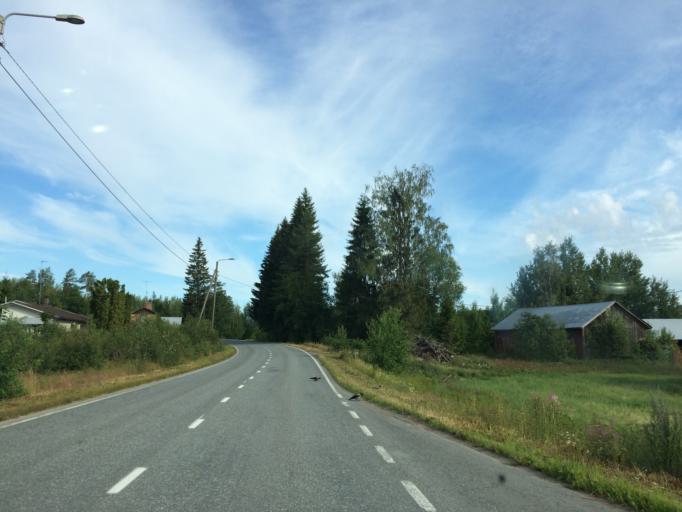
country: FI
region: Haeme
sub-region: Haemeenlinna
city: Janakkala
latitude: 60.9253
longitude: 24.5857
